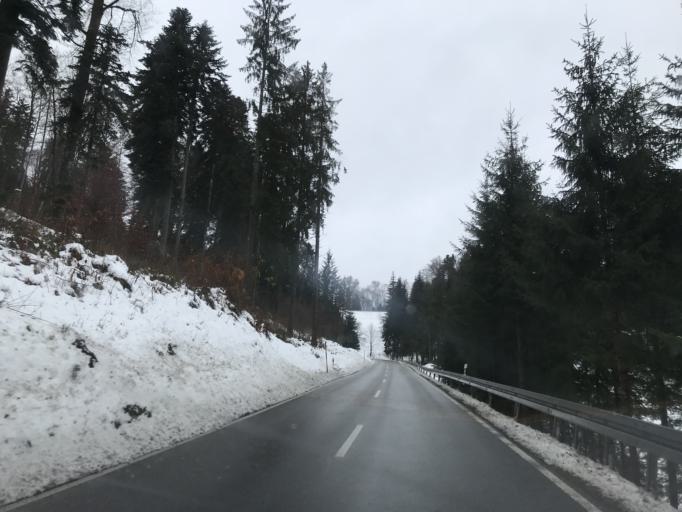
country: DE
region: Baden-Wuerttemberg
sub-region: Freiburg Region
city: Hasel
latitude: 47.6922
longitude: 7.8923
